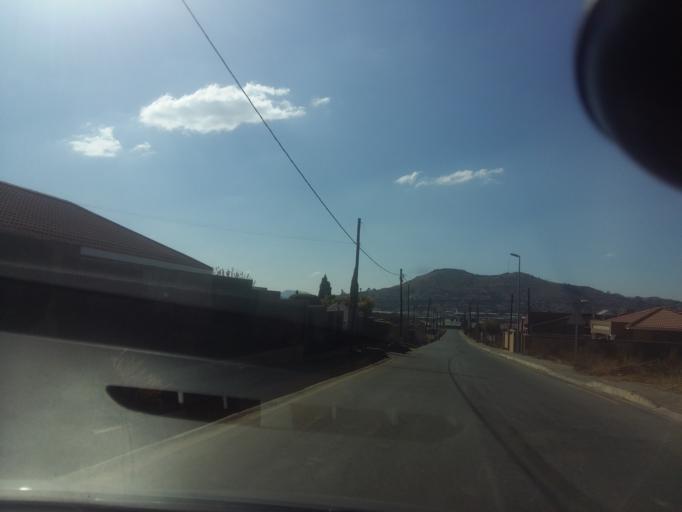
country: LS
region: Maseru
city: Maseru
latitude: -29.3470
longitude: 27.4499
